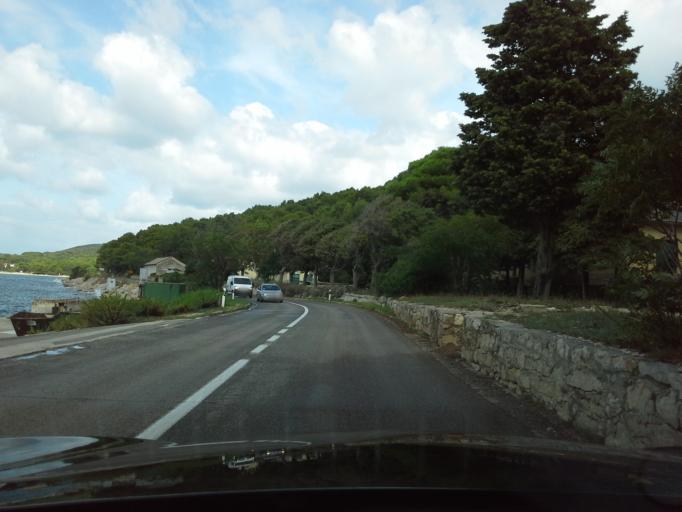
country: HR
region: Primorsko-Goranska
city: Mali Losinj
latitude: 44.5600
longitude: 14.4377
